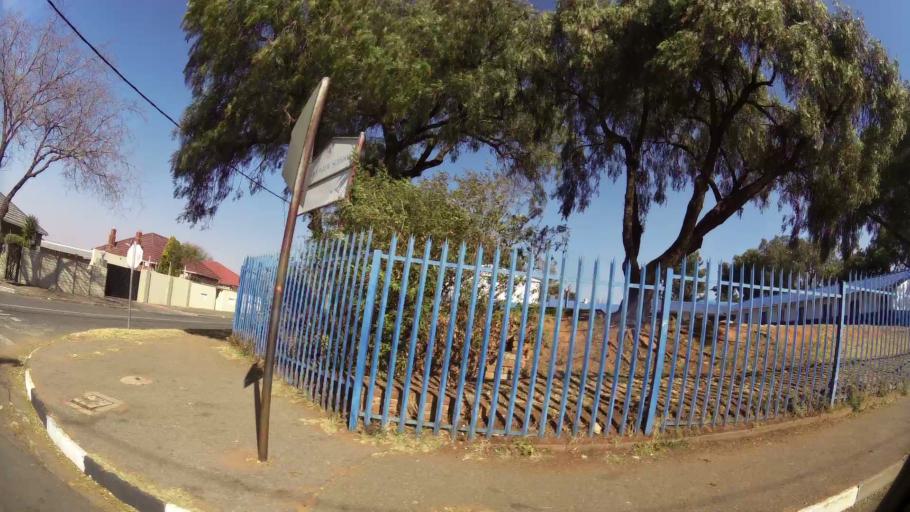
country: ZA
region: Gauteng
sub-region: City of Johannesburg Metropolitan Municipality
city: Johannesburg
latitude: -26.2586
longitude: 28.0534
